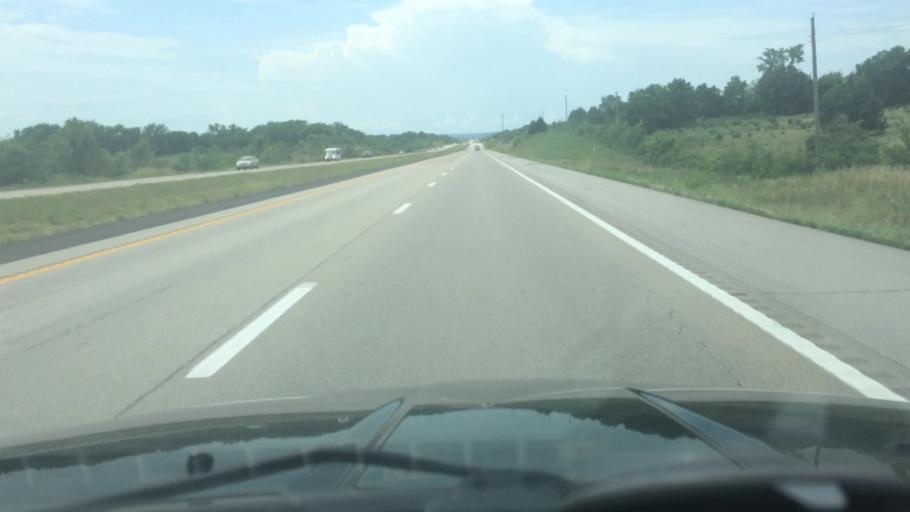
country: US
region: Missouri
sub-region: Polk County
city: Humansville
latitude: 37.7673
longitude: -93.5622
